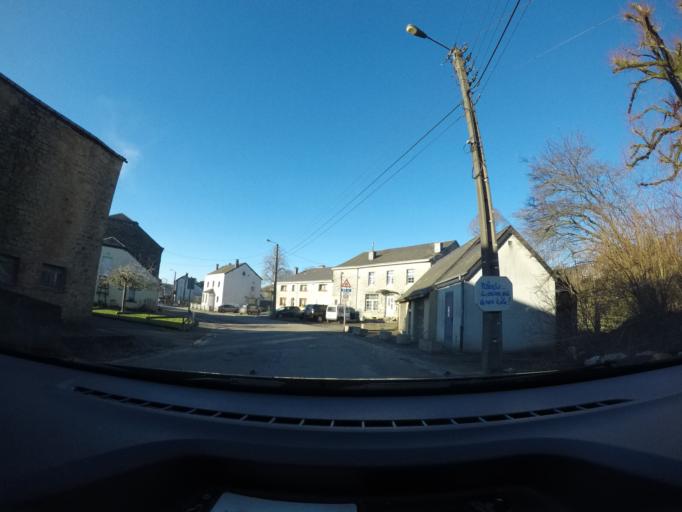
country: BE
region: Wallonia
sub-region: Province du Luxembourg
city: Bertrix
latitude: 49.8347
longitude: 5.3058
